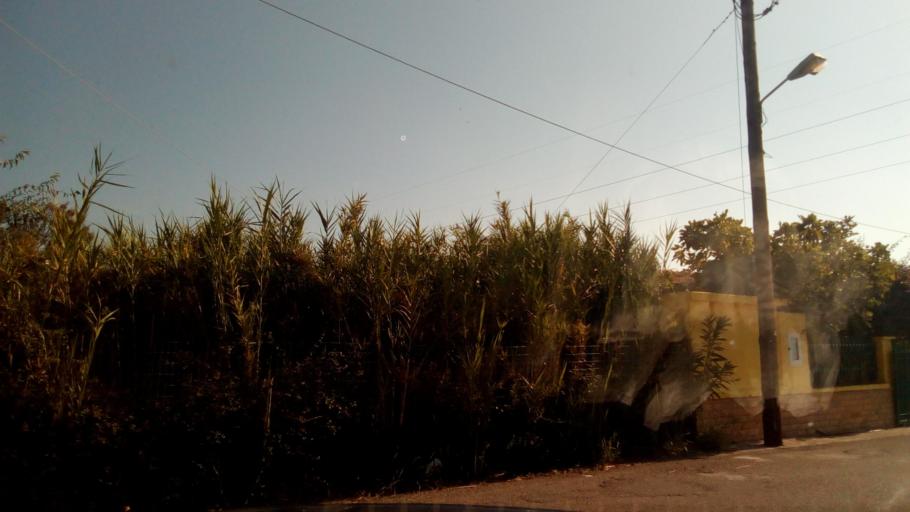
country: GR
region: West Greece
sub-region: Nomos Aitolias kai Akarnanias
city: Antirrio
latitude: 38.3394
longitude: 21.7675
